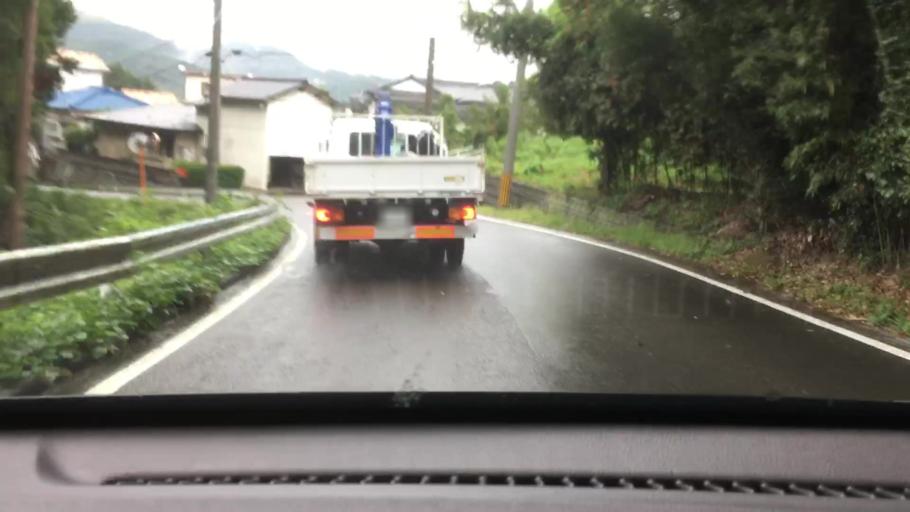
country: JP
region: Nagasaki
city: Togitsu
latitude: 32.8576
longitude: 129.7784
